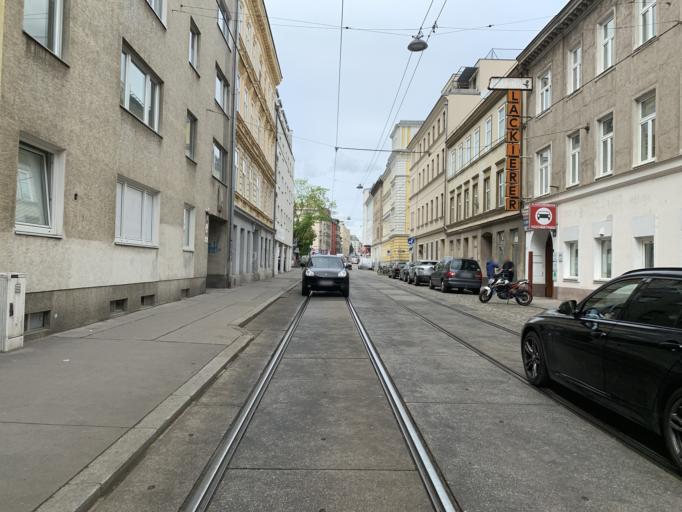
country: AT
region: Vienna
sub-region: Wien Stadt
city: Vienna
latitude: 48.2234
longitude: 16.3381
